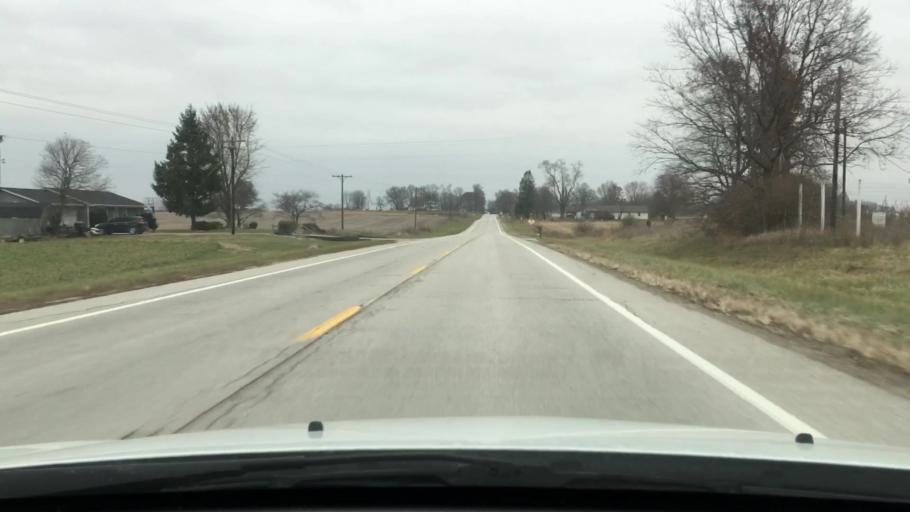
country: US
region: Illinois
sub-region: Pike County
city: Pittsfield
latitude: 39.5370
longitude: -90.9206
